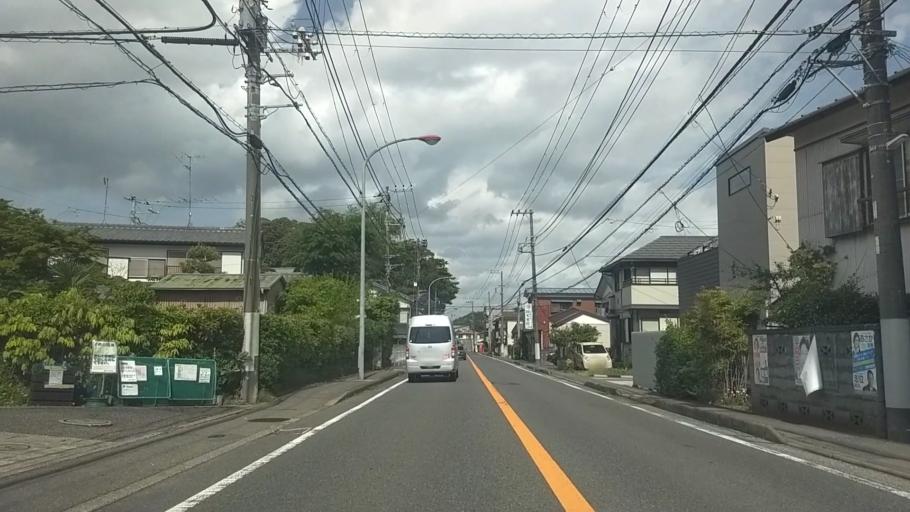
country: JP
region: Kanagawa
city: Zushi
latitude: 35.2976
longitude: 139.6099
